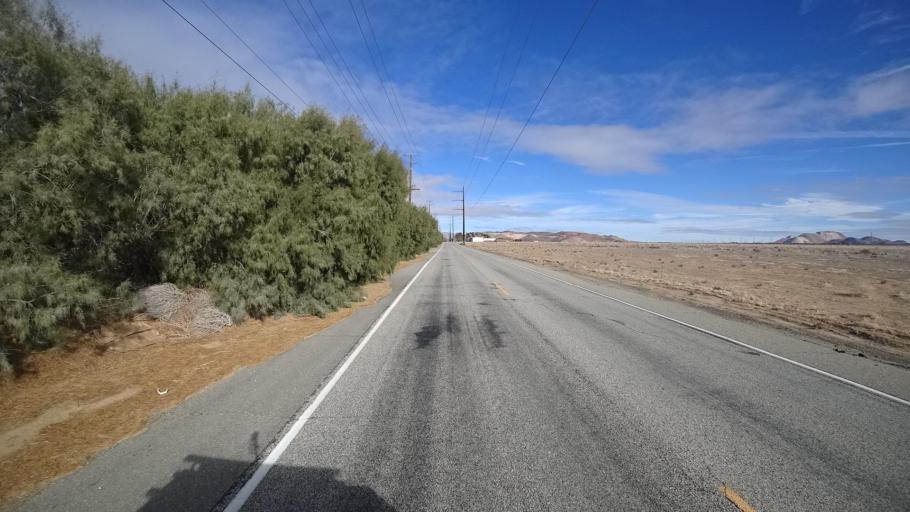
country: US
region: California
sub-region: Kern County
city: Rosamond
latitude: 34.9156
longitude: -118.2914
